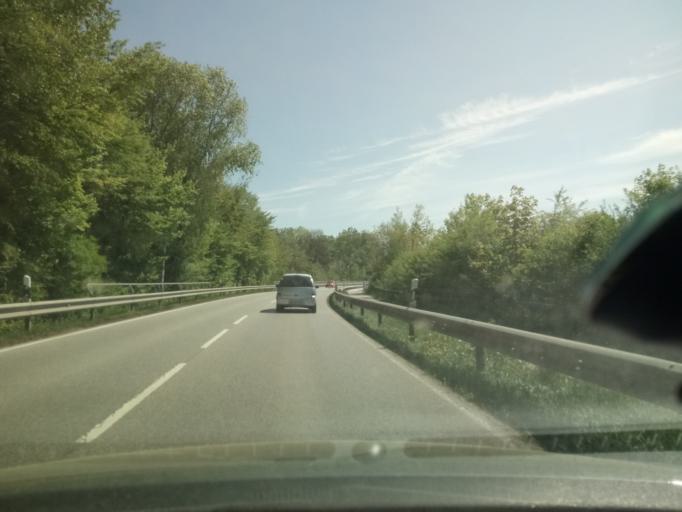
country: DE
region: Bavaria
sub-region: Upper Bavaria
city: Kraiburg am Inn
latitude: 48.1939
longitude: 12.4274
